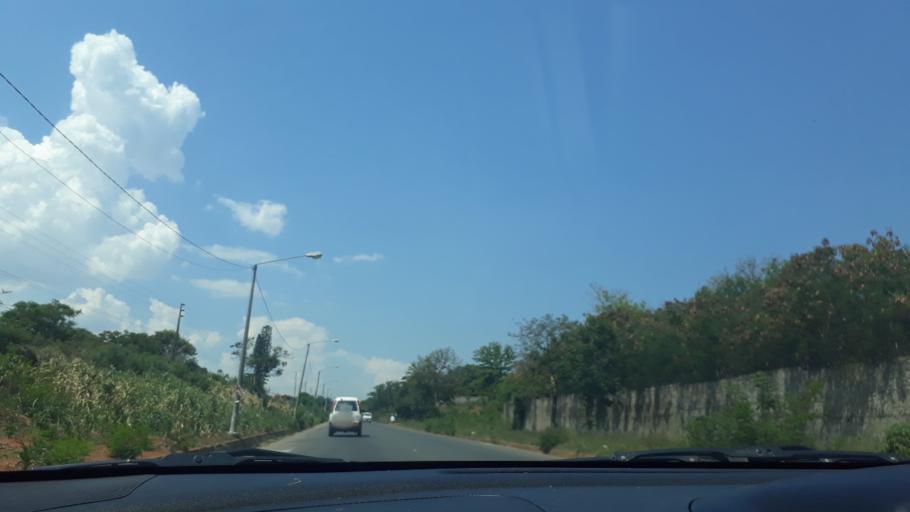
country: MZ
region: Maputo
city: Matola
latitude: -25.9642
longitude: 32.4467
